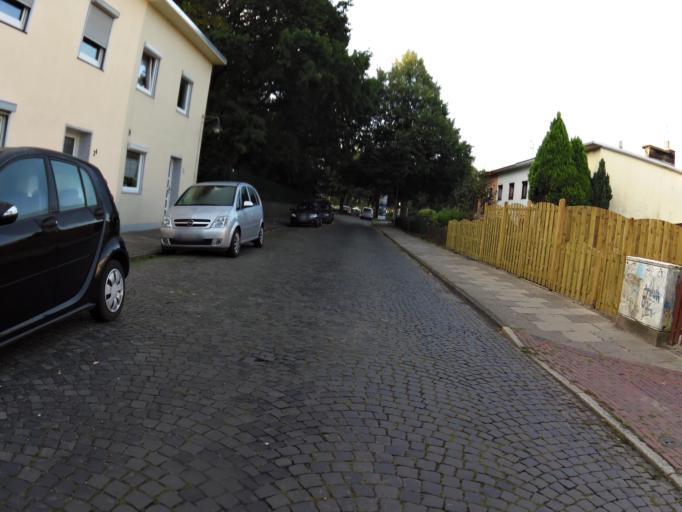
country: DE
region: Bremen
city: Bremen
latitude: 53.0872
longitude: 8.7594
